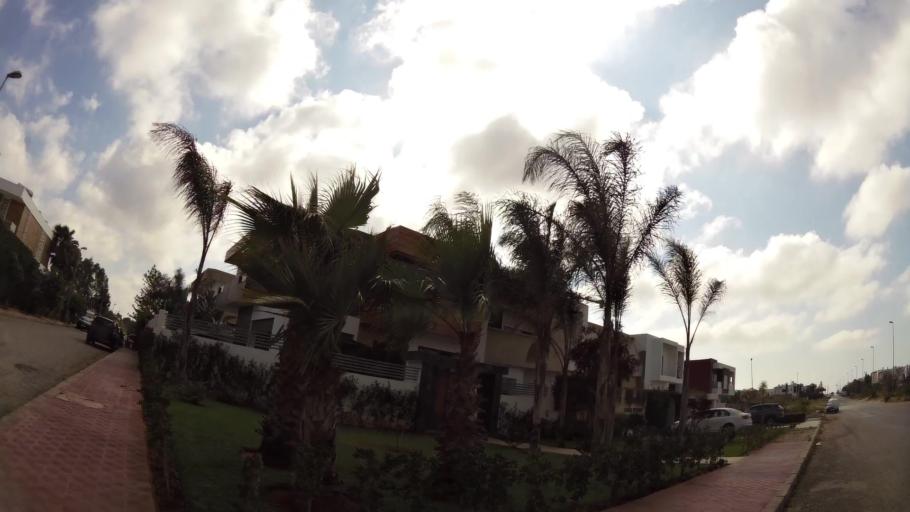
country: MA
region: Rabat-Sale-Zemmour-Zaer
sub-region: Skhirate-Temara
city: Temara
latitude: 33.9505
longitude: -6.8759
